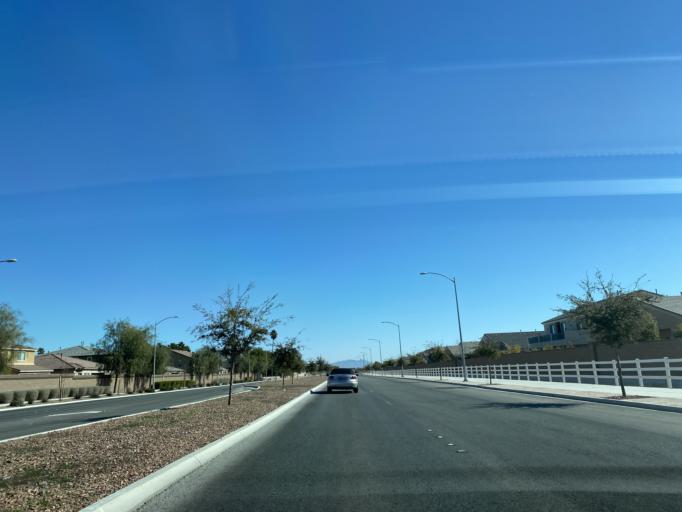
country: US
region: Nevada
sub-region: Clark County
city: North Las Vegas
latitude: 36.3051
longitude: -115.2556
